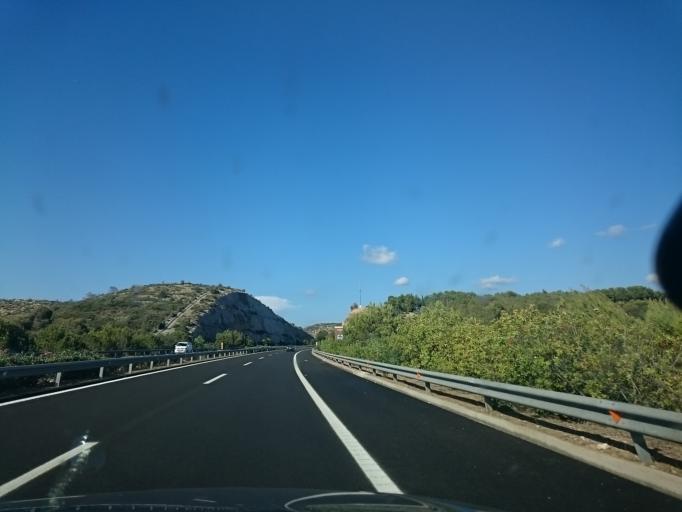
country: ES
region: Catalonia
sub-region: Provincia de Barcelona
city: Vilanova i la Geltru
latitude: 41.2459
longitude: 1.6927
